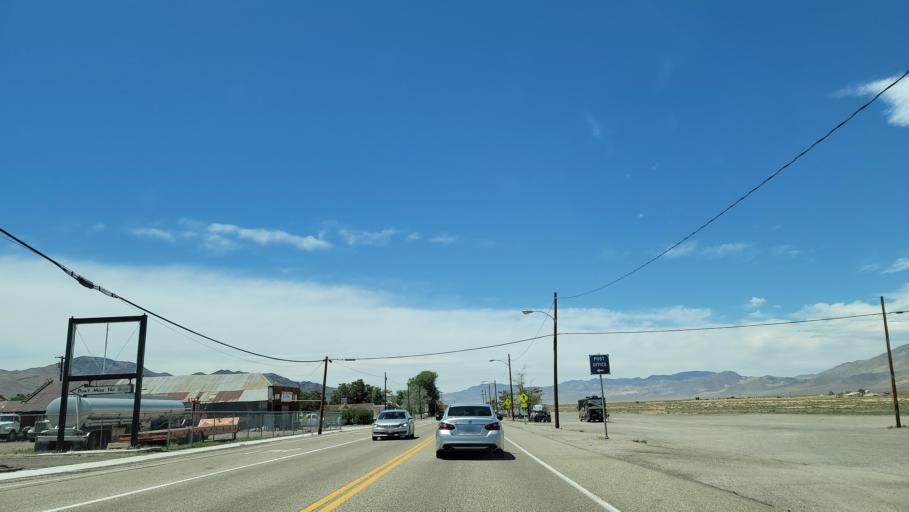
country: US
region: Nevada
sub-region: Mineral County
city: Hawthorne
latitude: 38.3916
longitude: -118.1093
